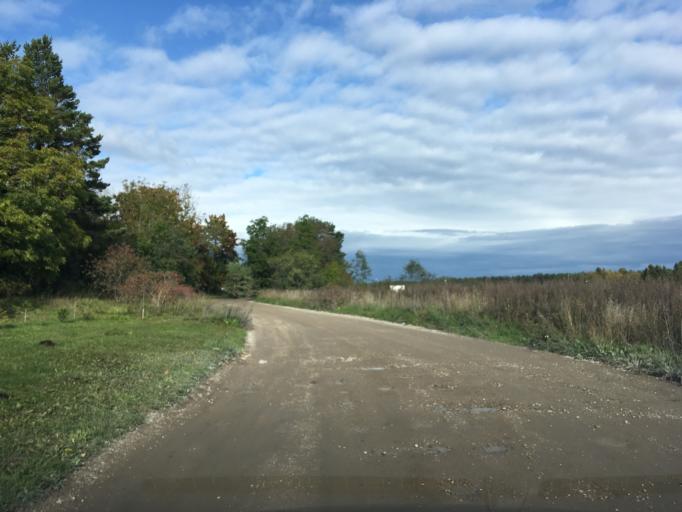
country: EE
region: Harju
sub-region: Saue vald
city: Laagri
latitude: 59.3397
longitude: 24.6498
